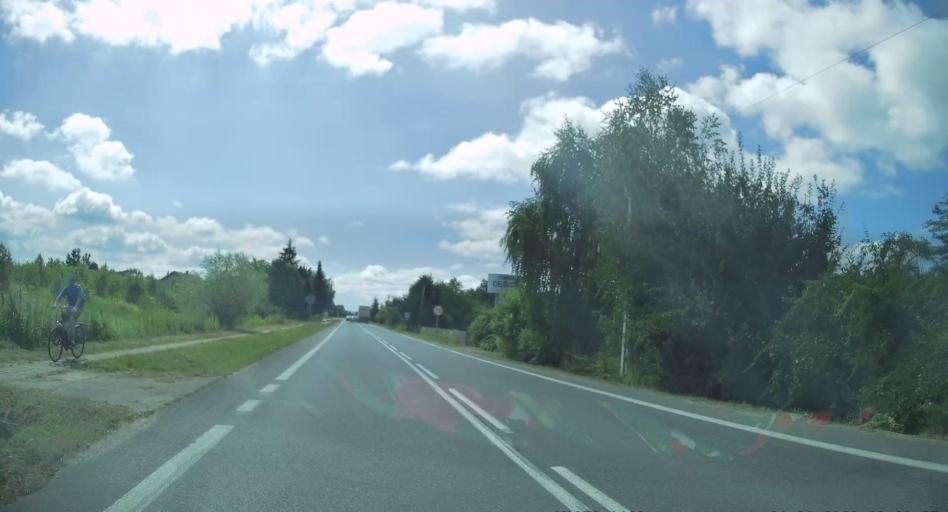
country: PL
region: Subcarpathian Voivodeship
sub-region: Powiat mielecki
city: Przeclaw
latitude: 50.1669
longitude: 21.4883
